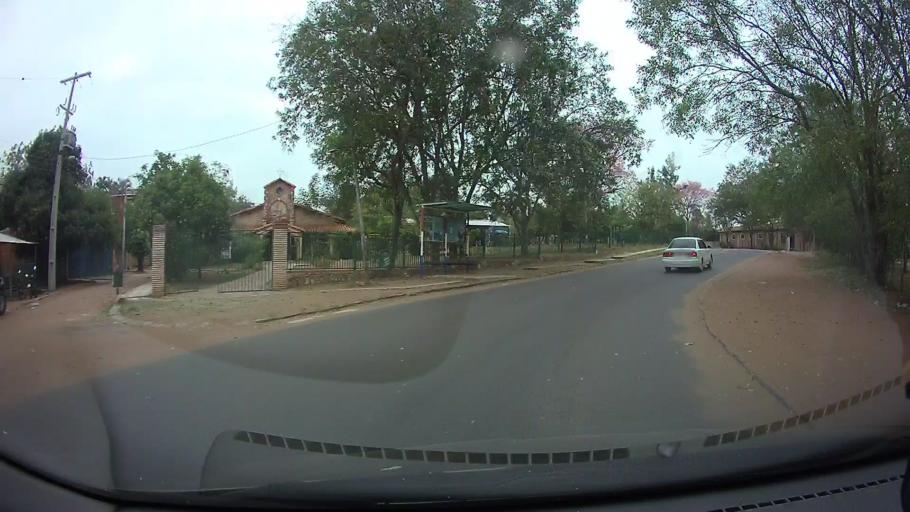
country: PY
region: Central
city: Limpio
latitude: -25.1512
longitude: -57.4566
